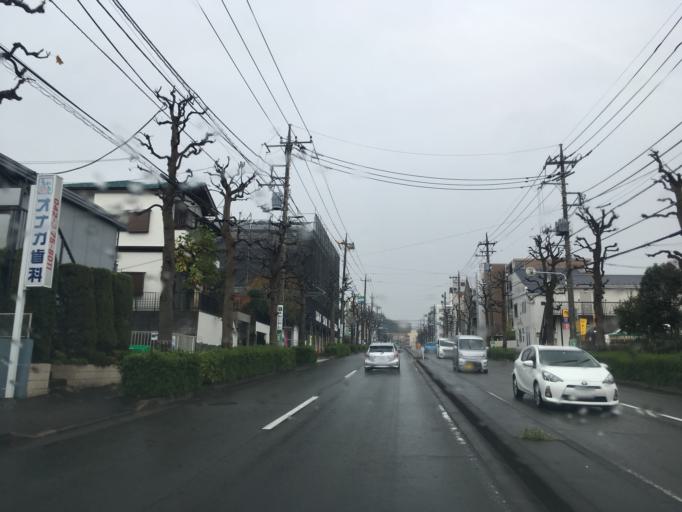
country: JP
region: Tokyo
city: Hino
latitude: 35.6345
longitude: 139.4505
